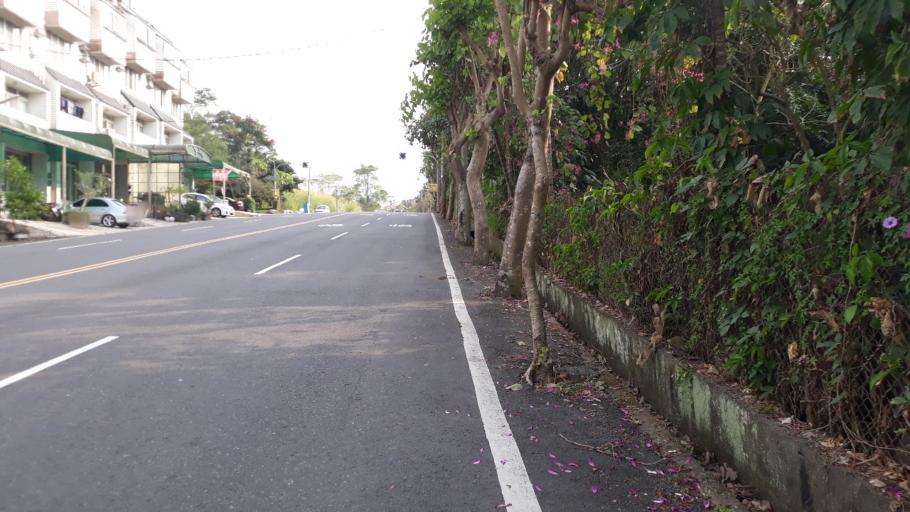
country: TW
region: Taiwan
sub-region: Chiayi
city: Jiayi Shi
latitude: 23.4302
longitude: 120.5157
